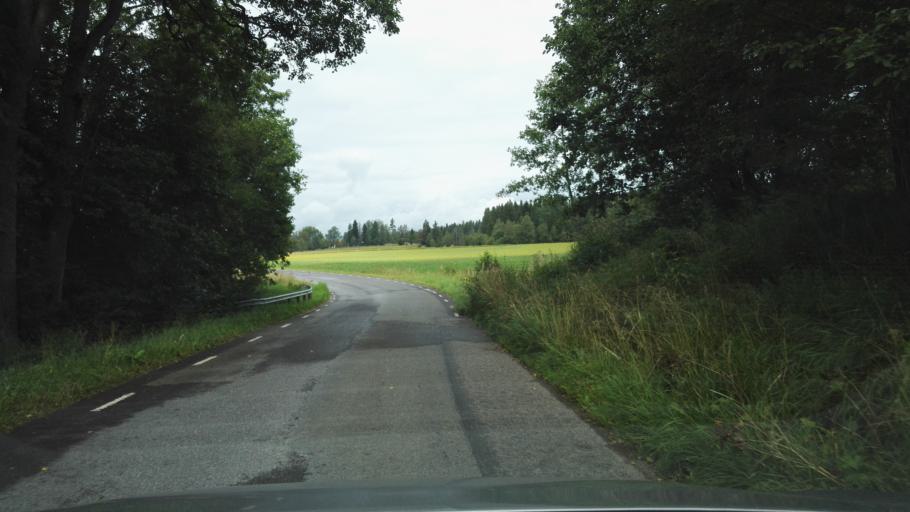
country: SE
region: Kronoberg
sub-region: Vaxjo Kommun
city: Rottne
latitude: 57.1710
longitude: 14.7887
